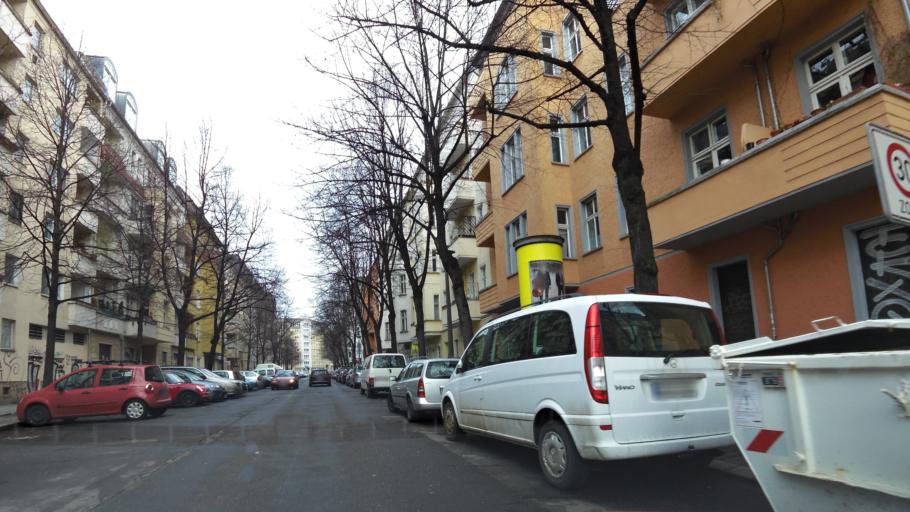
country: DE
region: Berlin
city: Friedrichshain Bezirk
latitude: 52.5124
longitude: 13.4701
